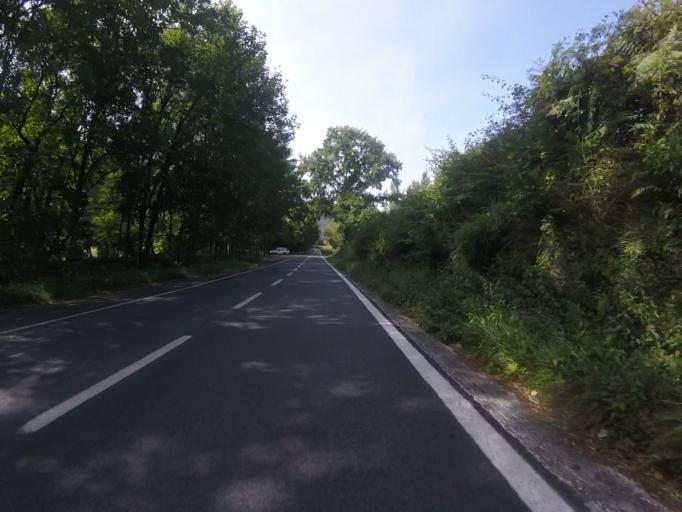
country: ES
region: Navarre
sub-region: Provincia de Navarra
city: Elgorriaga
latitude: 43.1329
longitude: -1.6987
